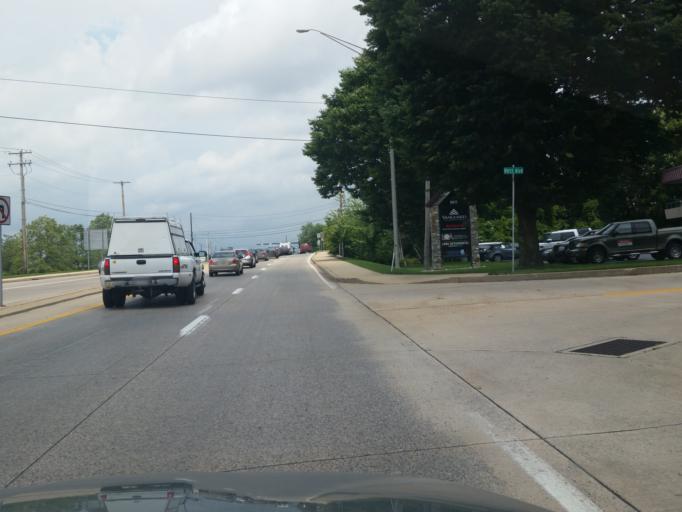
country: US
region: Pennsylvania
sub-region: Lancaster County
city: Lancaster
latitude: 40.0717
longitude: -76.3182
